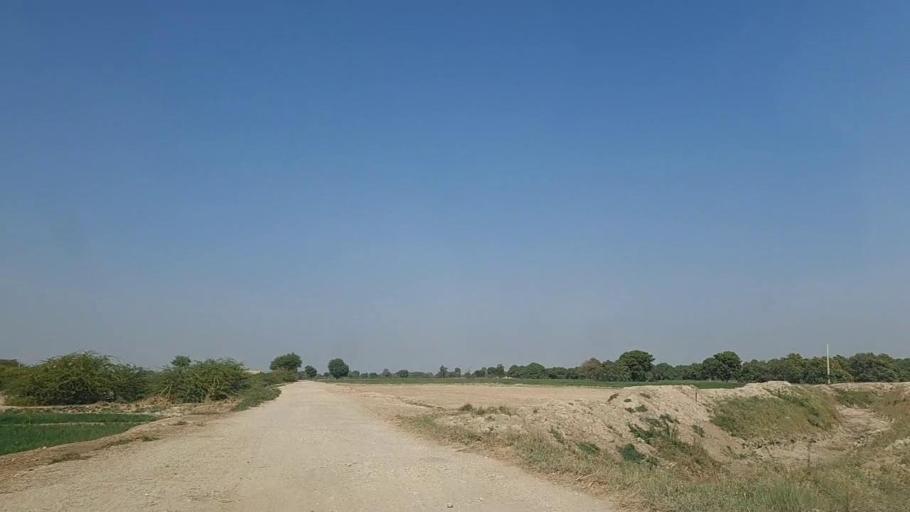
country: PK
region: Sindh
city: Naukot
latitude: 24.8526
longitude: 69.4156
